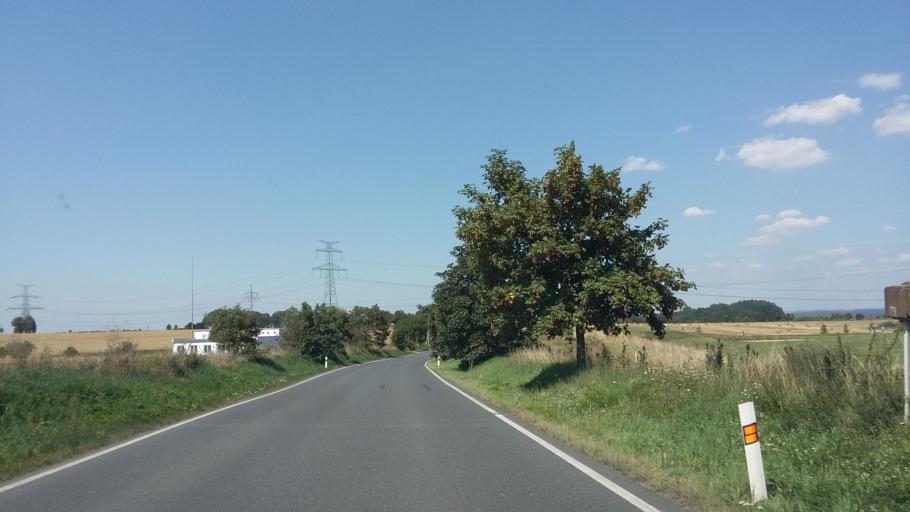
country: CZ
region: Central Bohemia
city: Zelenec
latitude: 50.1485
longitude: 14.6888
